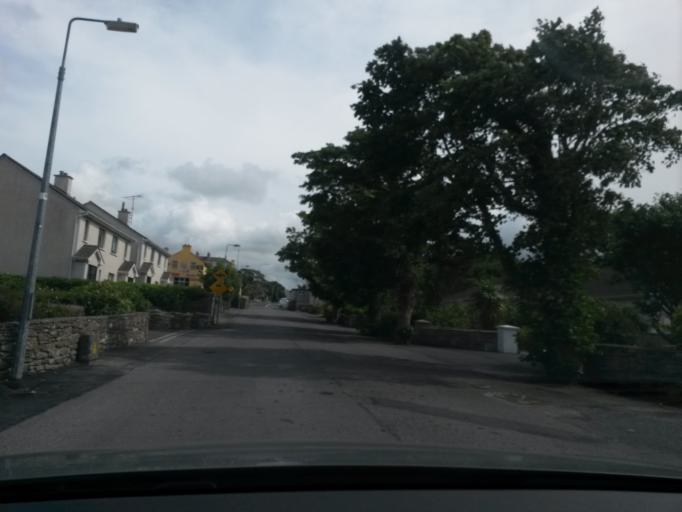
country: IE
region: Connaught
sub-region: Sligo
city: Sligo
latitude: 54.4310
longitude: -8.4549
